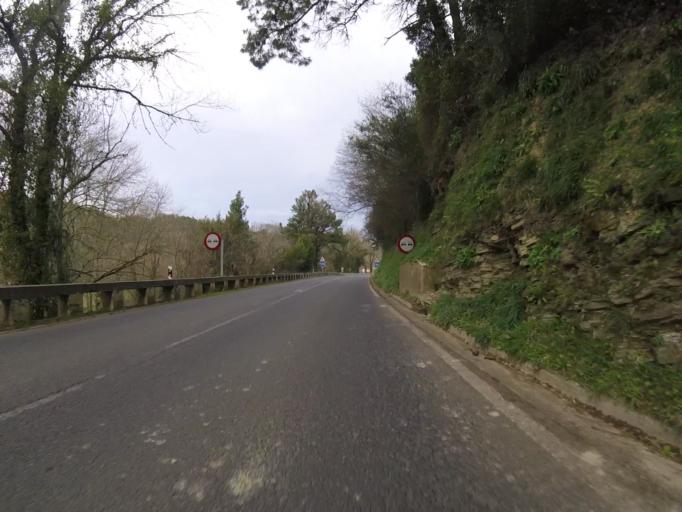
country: ES
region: Basque Country
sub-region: Provincia de Guipuzcoa
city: Aizarnazabal
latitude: 43.2708
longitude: -2.2320
